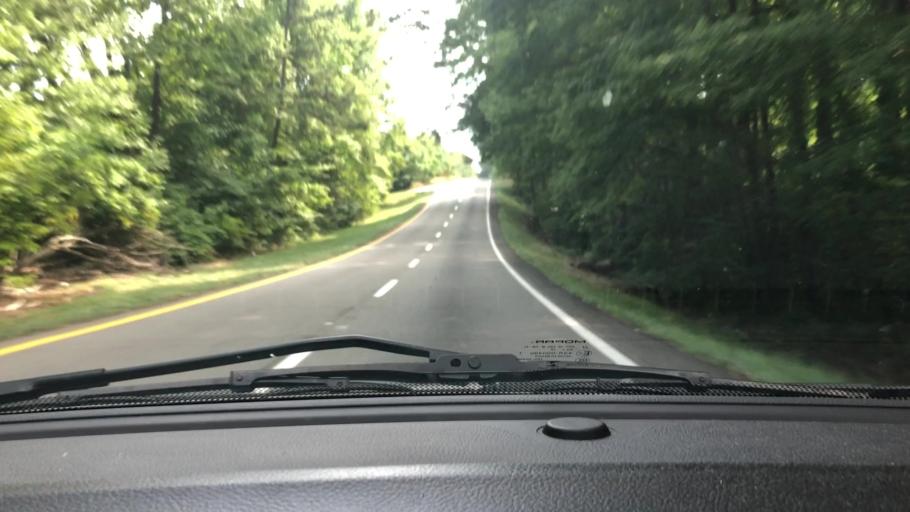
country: US
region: Virginia
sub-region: Henry County
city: Horse Pasture
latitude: 36.5667
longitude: -79.8755
